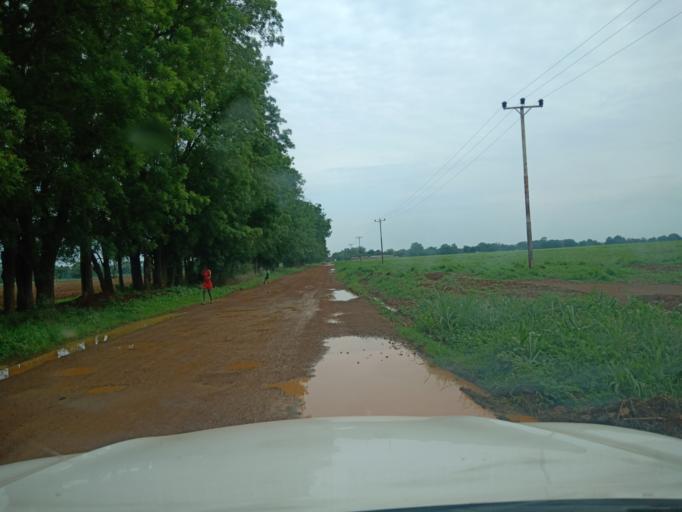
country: ET
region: Gambela
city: Gambela
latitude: 7.8957
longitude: 34.5505
